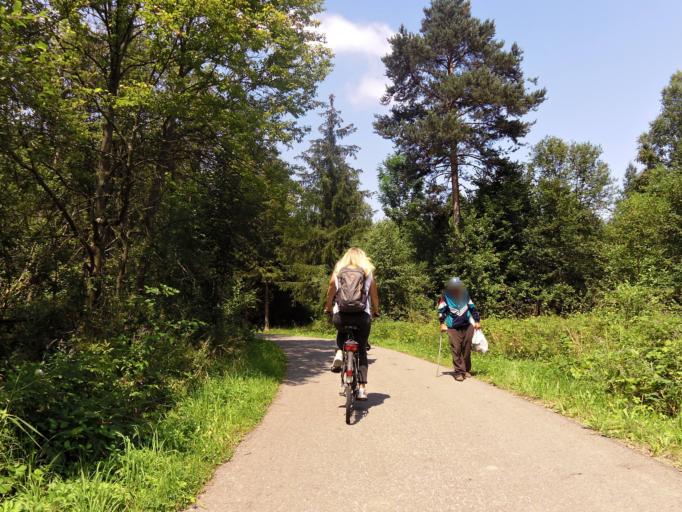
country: PL
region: Silesian Voivodeship
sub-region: Powiat zywiecki
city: Rajcza
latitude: 49.5270
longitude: 19.1073
